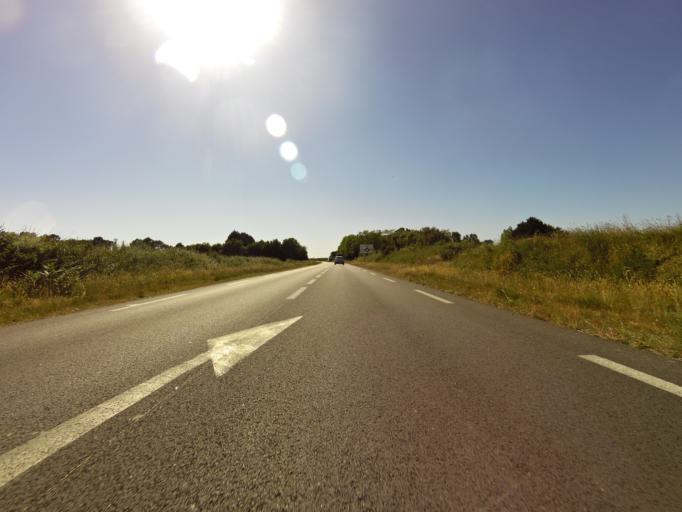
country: FR
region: Brittany
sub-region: Departement du Morbihan
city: Penestin
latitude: 47.4786
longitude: -2.4305
